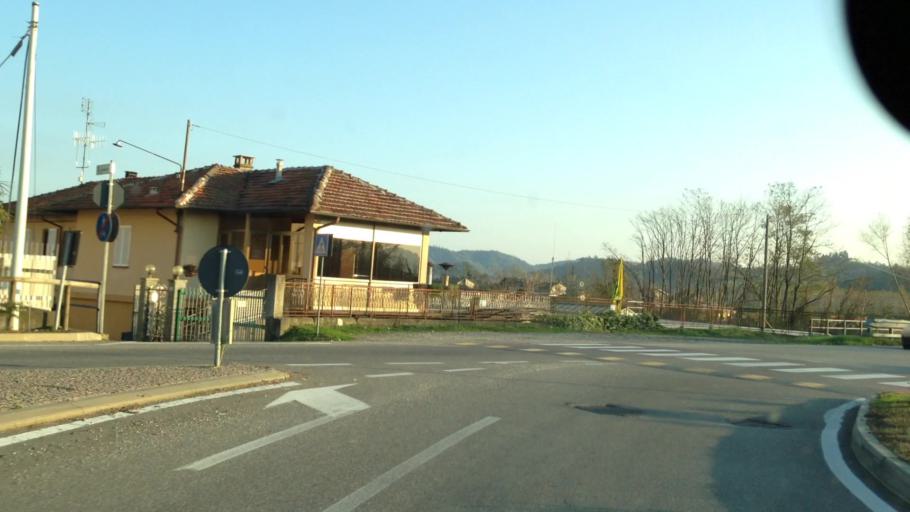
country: IT
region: Piedmont
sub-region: Provincia di Vercelli
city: Crescentino
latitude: 45.1853
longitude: 8.1009
